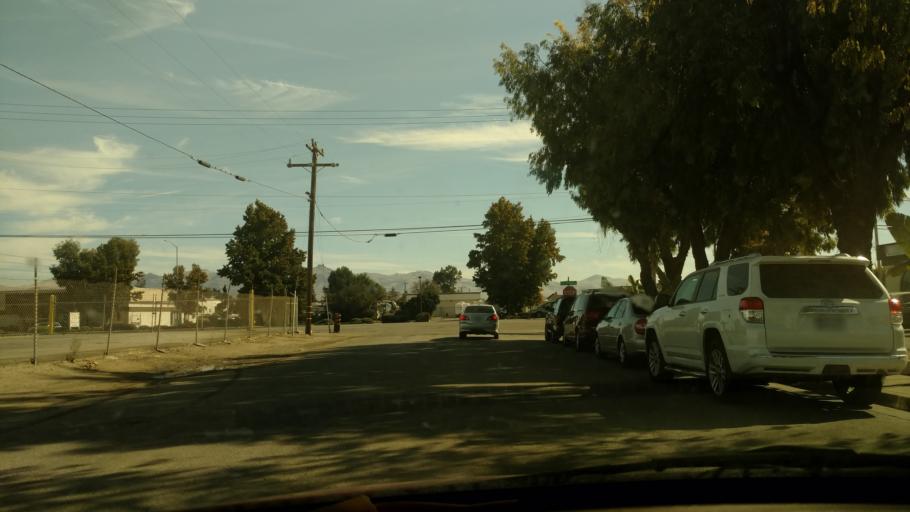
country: US
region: California
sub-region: San Benito County
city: Hollister
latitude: 36.8601
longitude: -121.4024
